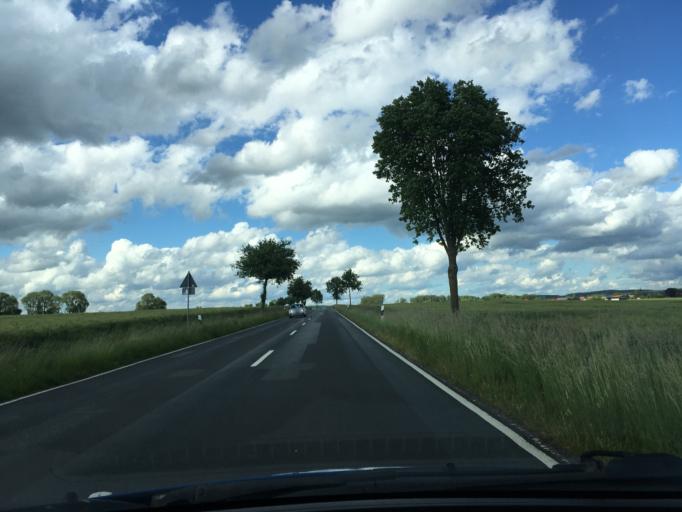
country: DE
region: Lower Saxony
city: Hardegsen
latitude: 51.6301
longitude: 9.8543
